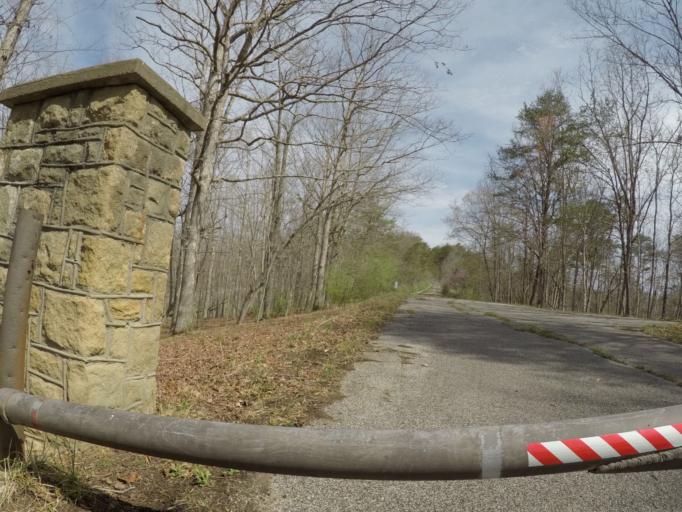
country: US
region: West Virginia
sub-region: Wayne County
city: Lavalette
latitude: 38.3109
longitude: -82.3519
